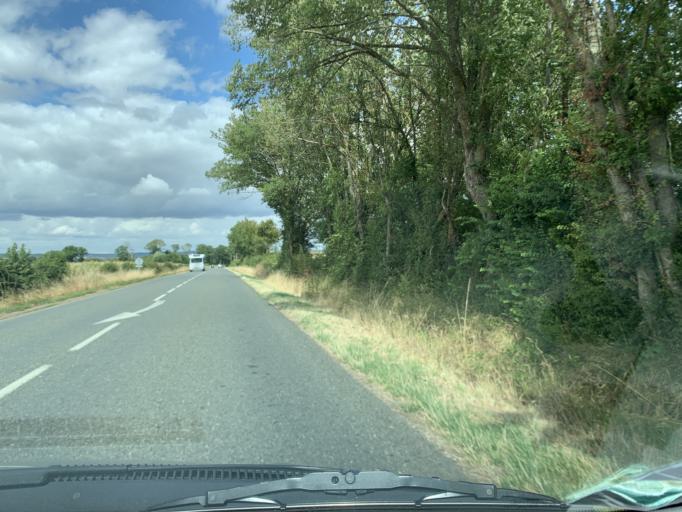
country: FR
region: Bourgogne
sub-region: Departement de la Nievre
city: Varzy
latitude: 47.3907
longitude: 3.4443
